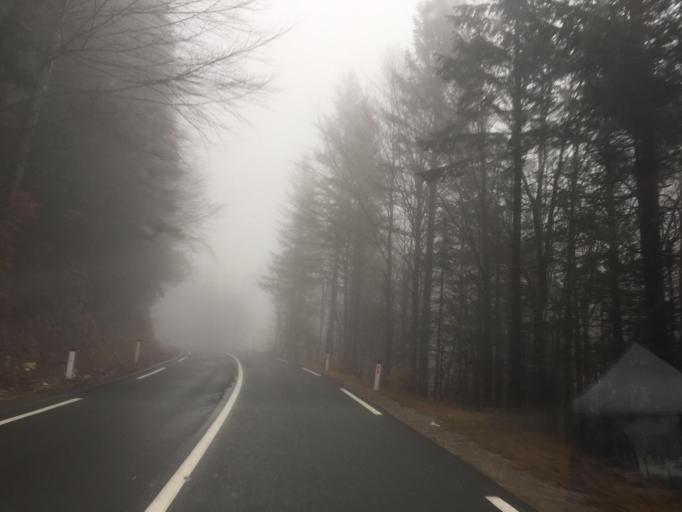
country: SI
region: Ajdovscina
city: Lokavec
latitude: 45.9442
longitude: 13.8722
